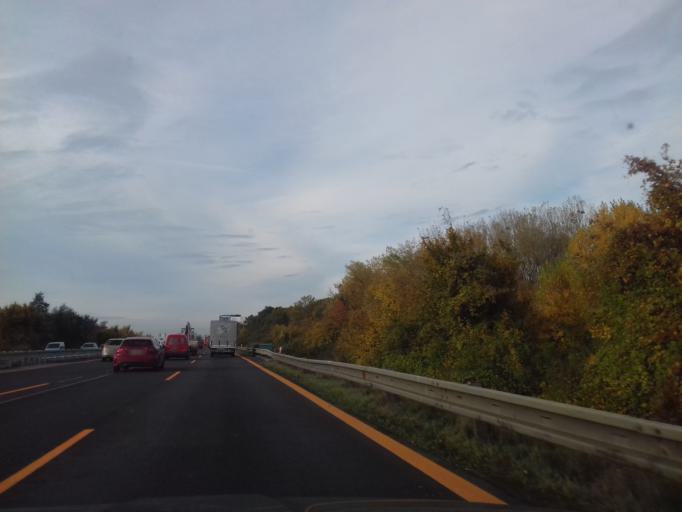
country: SK
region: Bratislavsky
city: Svaty Jur
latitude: 48.2082
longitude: 17.2457
